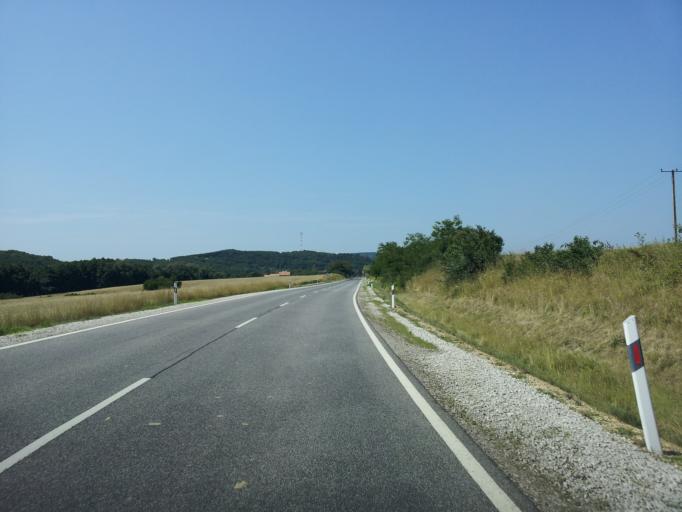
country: HU
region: Zala
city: Pacsa
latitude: 46.8253
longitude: 17.0133
